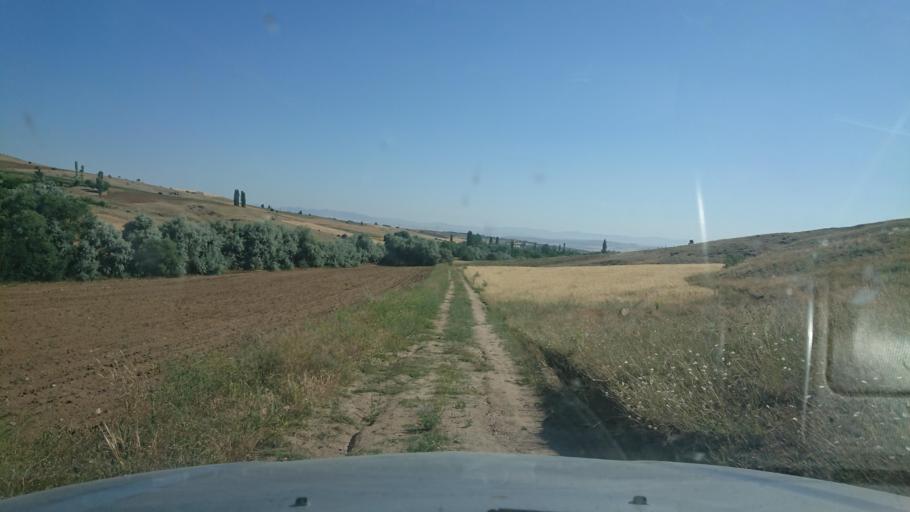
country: TR
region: Aksaray
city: Agacoren
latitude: 38.8429
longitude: 33.9261
